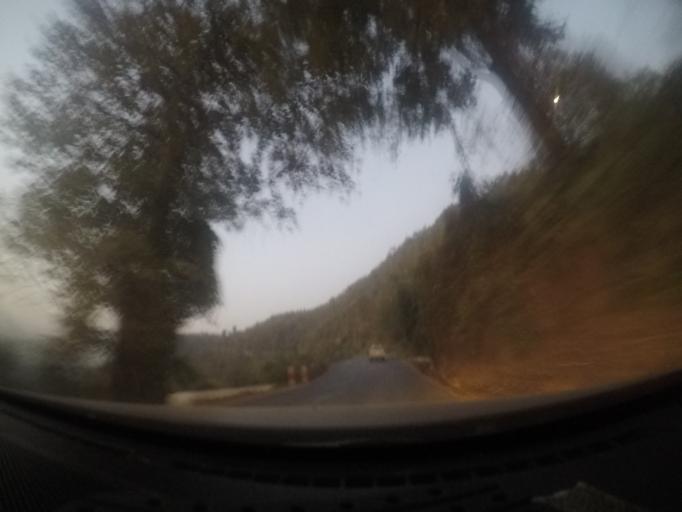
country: MM
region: Mandalay
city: Yamethin
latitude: 20.6962
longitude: 96.5078
